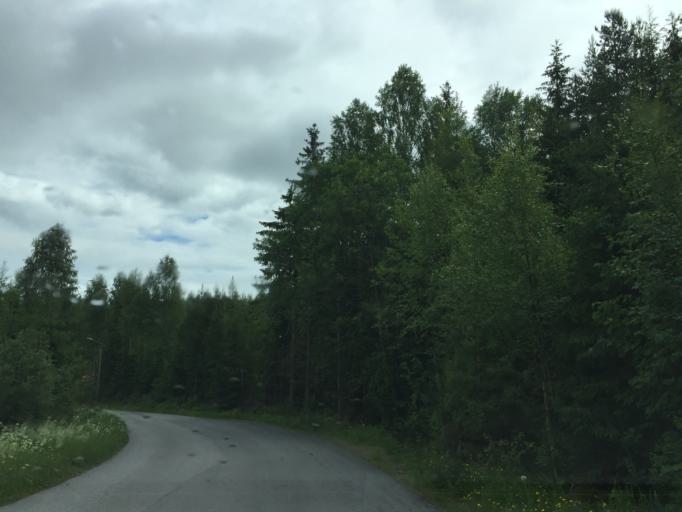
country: NO
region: Hedmark
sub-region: Kongsvinger
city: Kongsvinger
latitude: 60.1801
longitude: 11.9740
